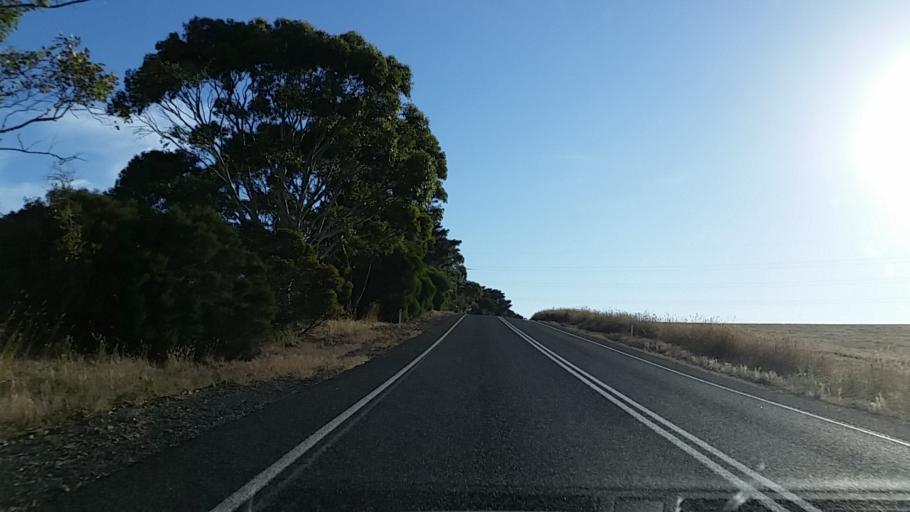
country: AU
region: South Australia
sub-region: Adelaide Hills
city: Birdwood
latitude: -34.7732
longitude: 139.1313
